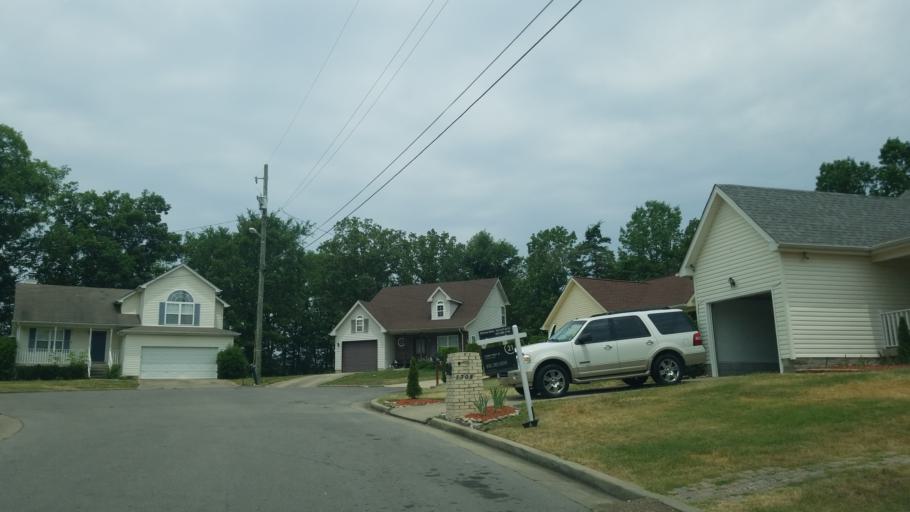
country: US
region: Tennessee
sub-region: Rutherford County
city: La Vergne
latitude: 36.0424
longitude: -86.5944
